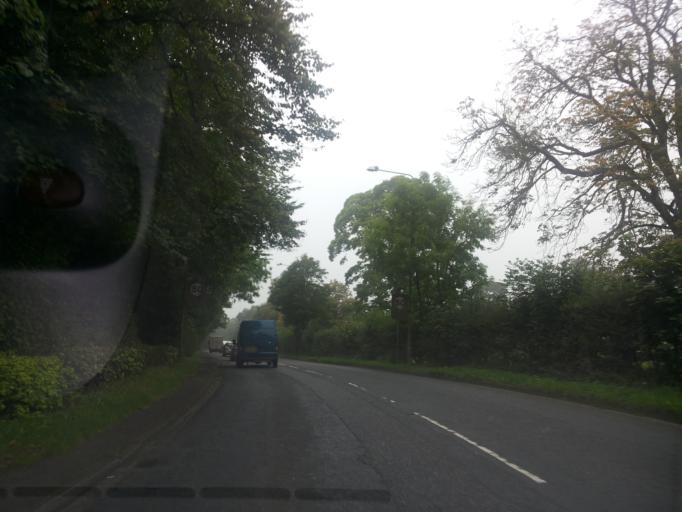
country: GB
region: England
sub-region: Lancashire
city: Clayton le Moors
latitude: 53.8052
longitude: -2.3676
